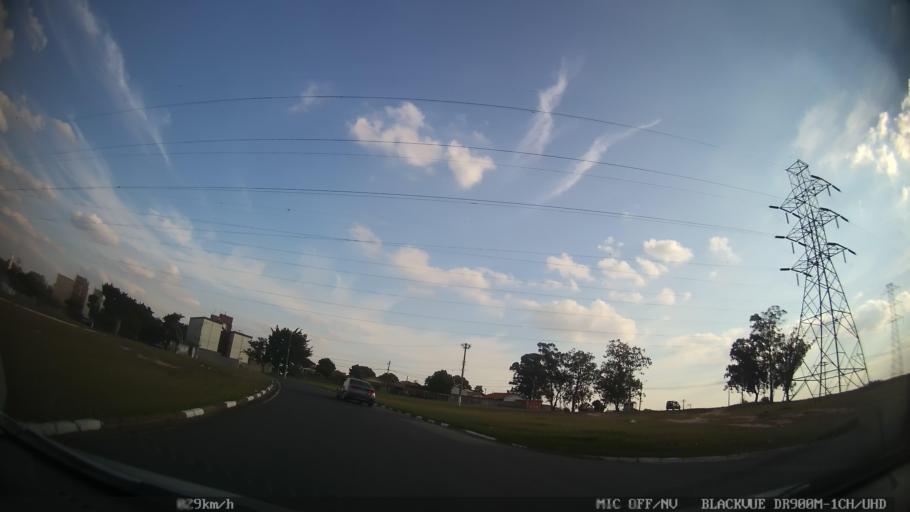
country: BR
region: Sao Paulo
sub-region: Hortolandia
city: Hortolandia
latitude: -22.8666
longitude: -47.1557
